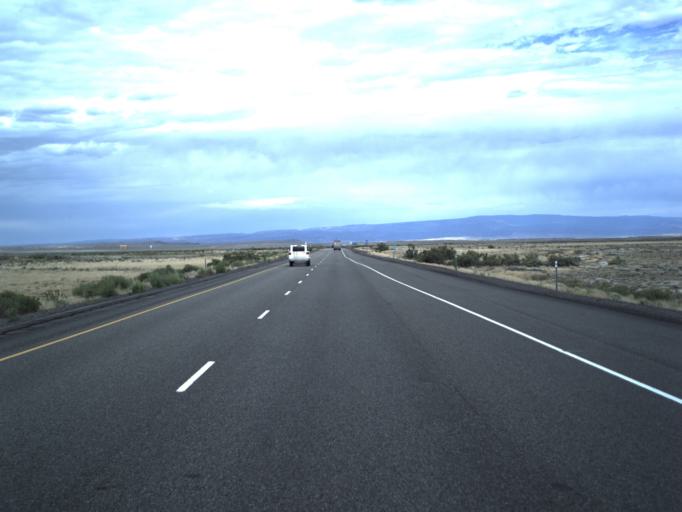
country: US
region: Utah
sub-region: Grand County
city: Moab
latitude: 38.9418
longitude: -109.6069
